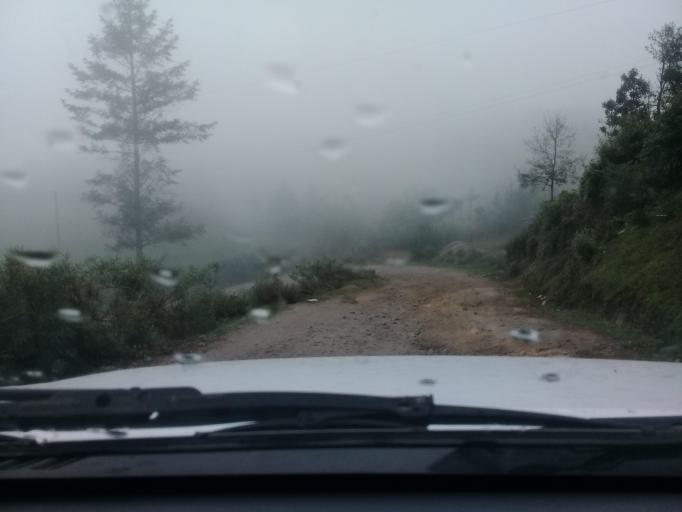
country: MX
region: Veracruz
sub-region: Mariano Escobedo
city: Texmola
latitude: 18.9586
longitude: -97.2203
